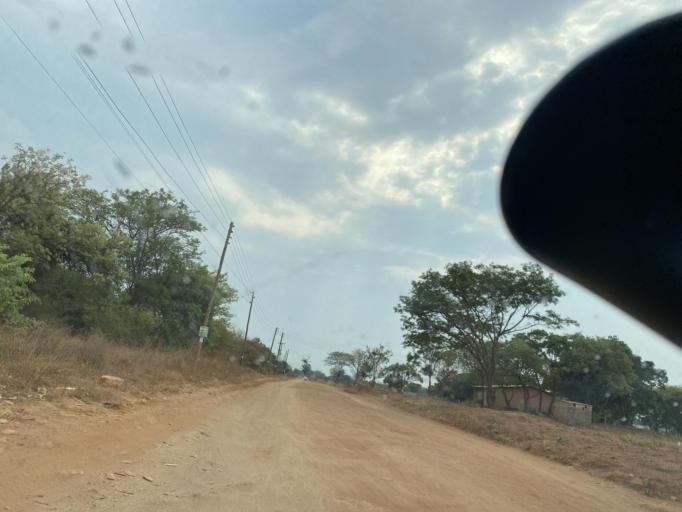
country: ZM
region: Lusaka
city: Lusaka
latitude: -15.2900
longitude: 28.2789
